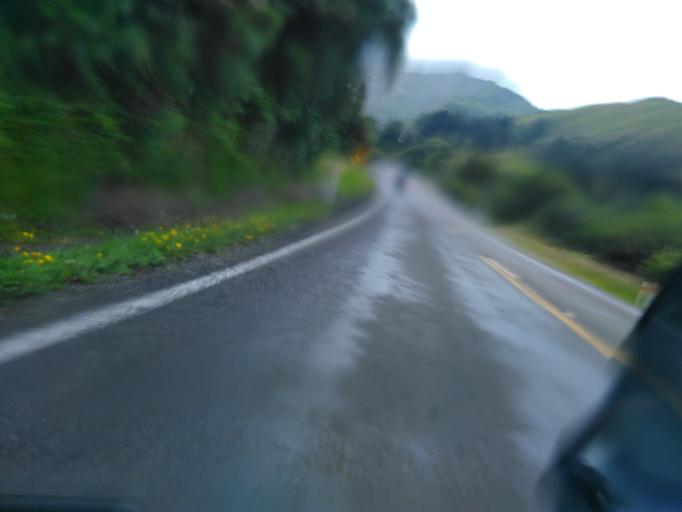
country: NZ
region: Bay of Plenty
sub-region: Opotiki District
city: Opotiki
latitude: -38.2547
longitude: 177.2986
